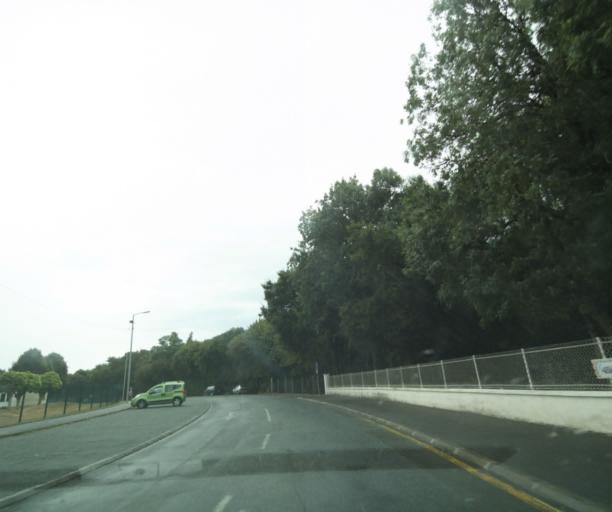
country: FR
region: Poitou-Charentes
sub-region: Departement de la Charente-Maritime
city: Tonnay-Charente
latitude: 45.9454
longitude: -0.9106
